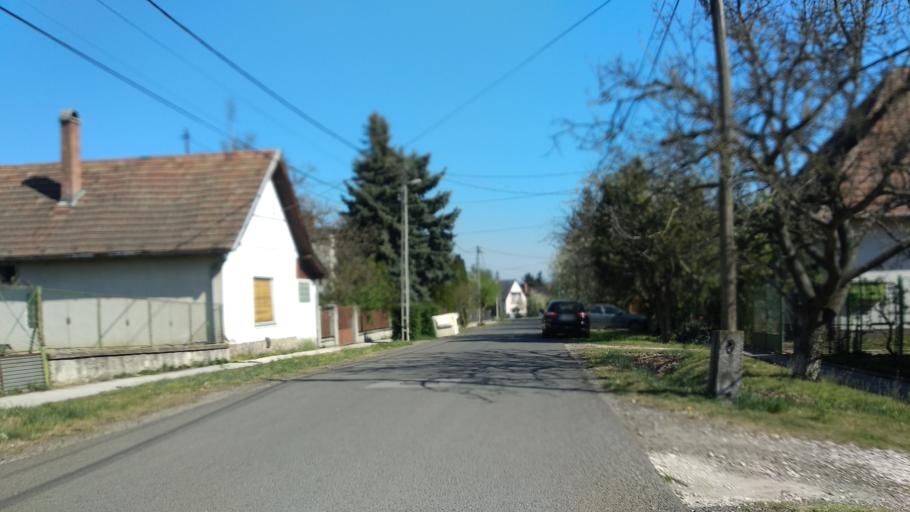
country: HU
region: Pest
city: Godollo
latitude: 47.5887
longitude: 19.3514
